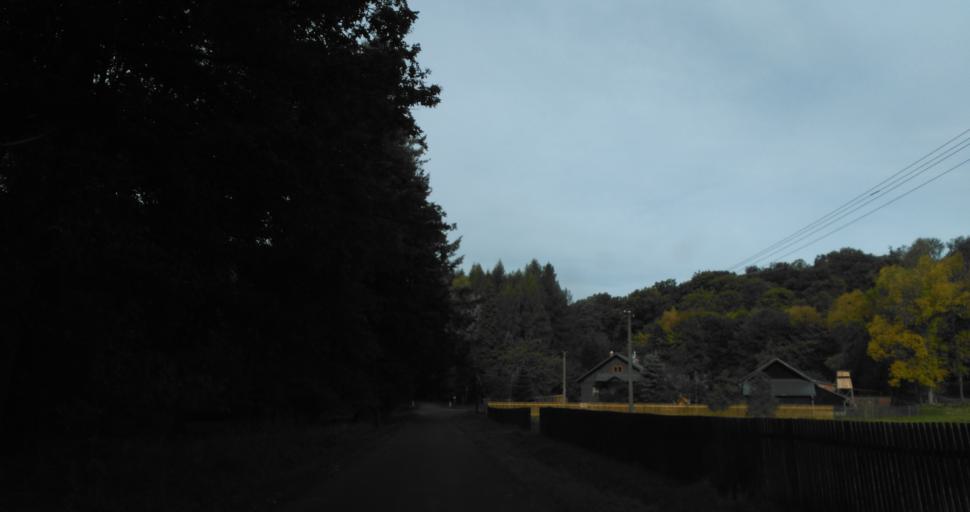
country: CZ
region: Plzensky
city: Zbiroh
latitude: 49.9236
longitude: 13.8058
